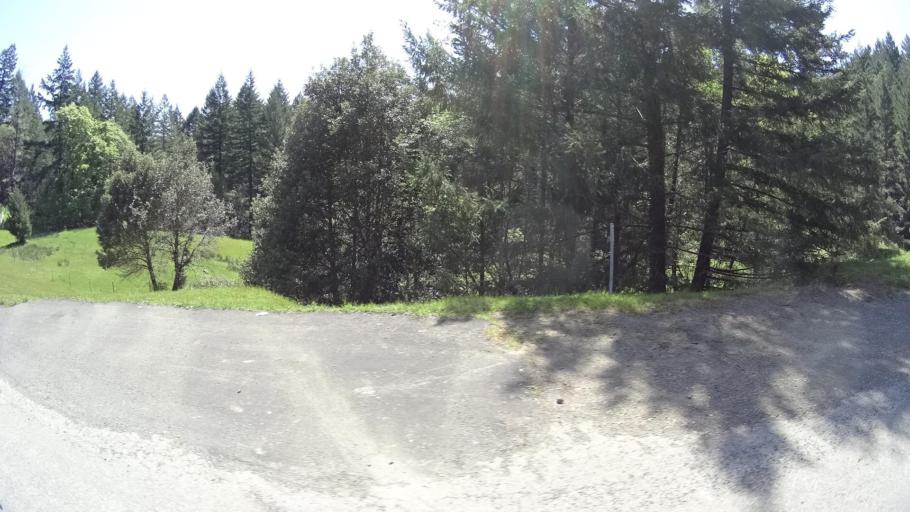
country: US
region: California
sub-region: Humboldt County
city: Redway
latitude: 40.1219
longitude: -123.6422
